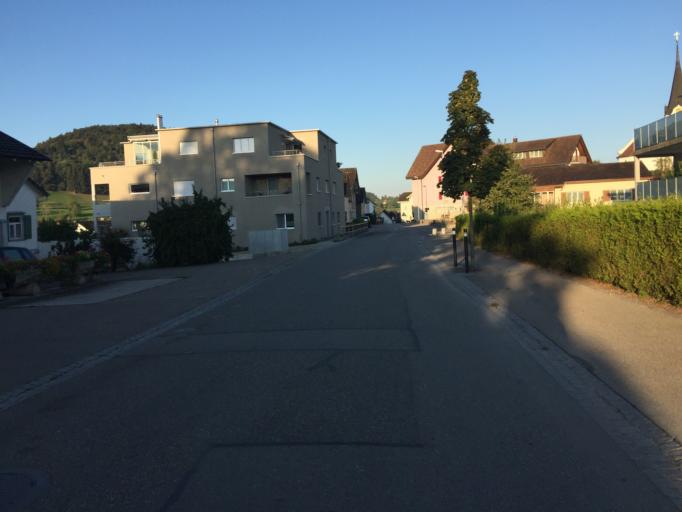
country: CH
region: Saint Gallen
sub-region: Wahlkreis Wil
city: Oberuzwil
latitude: 47.4204
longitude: 9.1389
